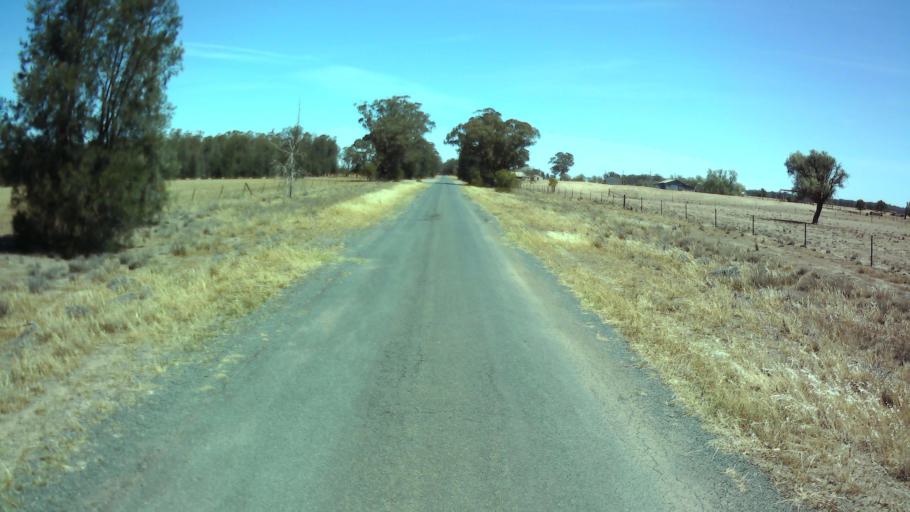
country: AU
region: New South Wales
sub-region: Weddin
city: Grenfell
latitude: -33.9016
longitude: 147.6862
